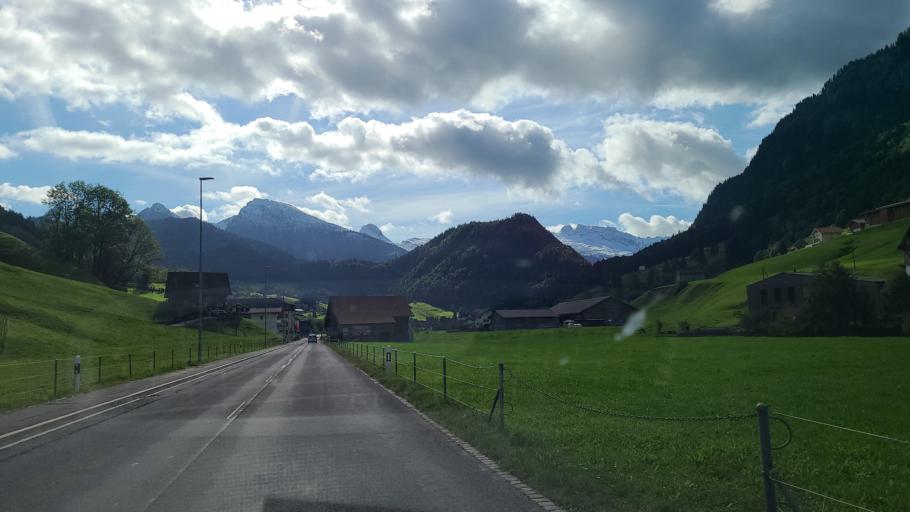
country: CH
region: Schwyz
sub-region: Bezirk March
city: Vorderthal
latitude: 47.1296
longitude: 8.8893
